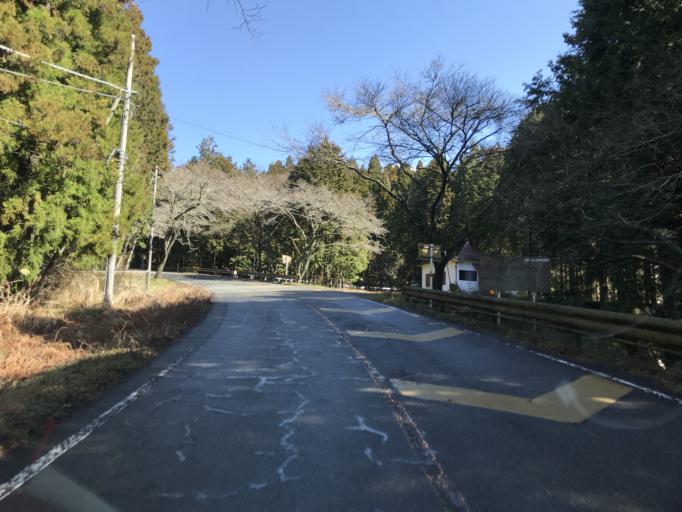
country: JP
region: Shizuoka
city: Fujinomiya
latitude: 35.2814
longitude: 138.6615
